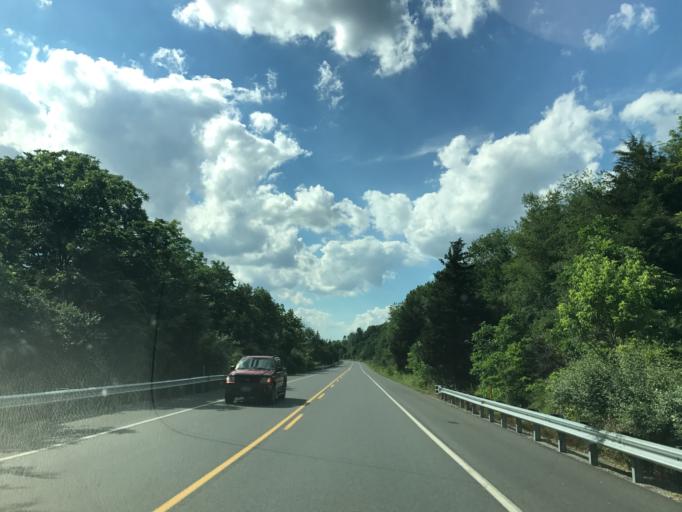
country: US
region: Pennsylvania
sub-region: York County
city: Parkville
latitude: 39.7780
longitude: -76.8809
